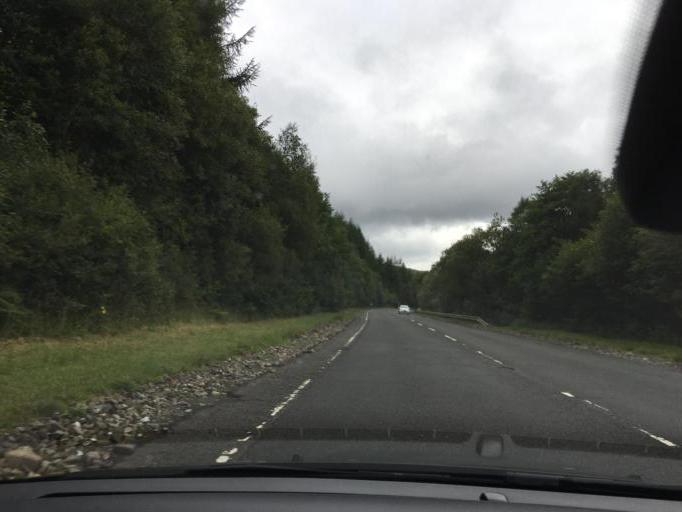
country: GB
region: Scotland
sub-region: Argyll and Bute
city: Garelochhead
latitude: 56.3580
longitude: -4.6797
